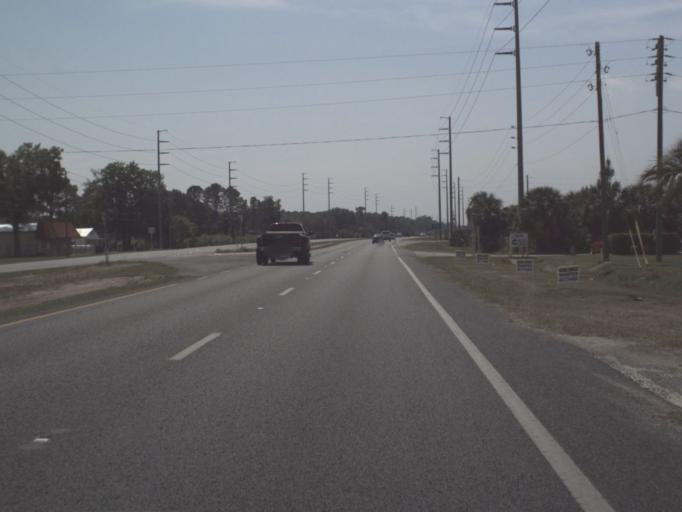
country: US
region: Florida
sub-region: Lake County
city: Eustis
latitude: 28.8916
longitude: -81.6870
